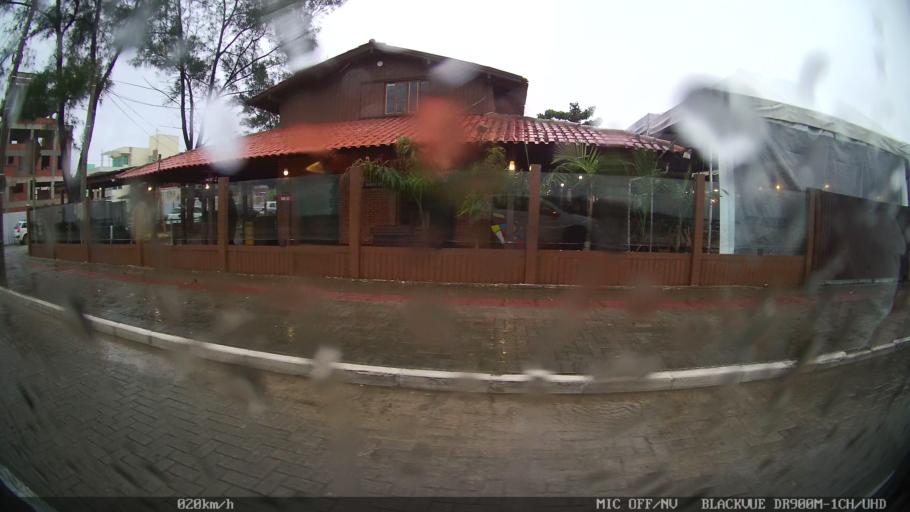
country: BR
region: Santa Catarina
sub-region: Balneario Camboriu
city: Balneario Camboriu
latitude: -26.9471
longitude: -48.6293
